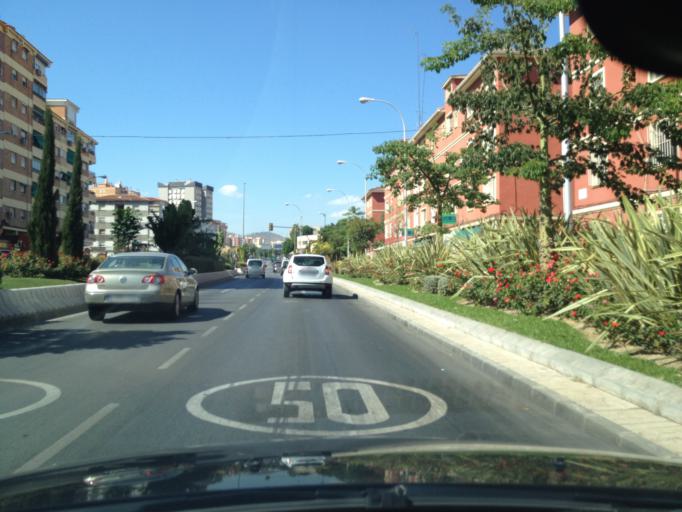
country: ES
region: Andalusia
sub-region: Provincia de Malaga
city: Malaga
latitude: 36.7104
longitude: -4.4451
